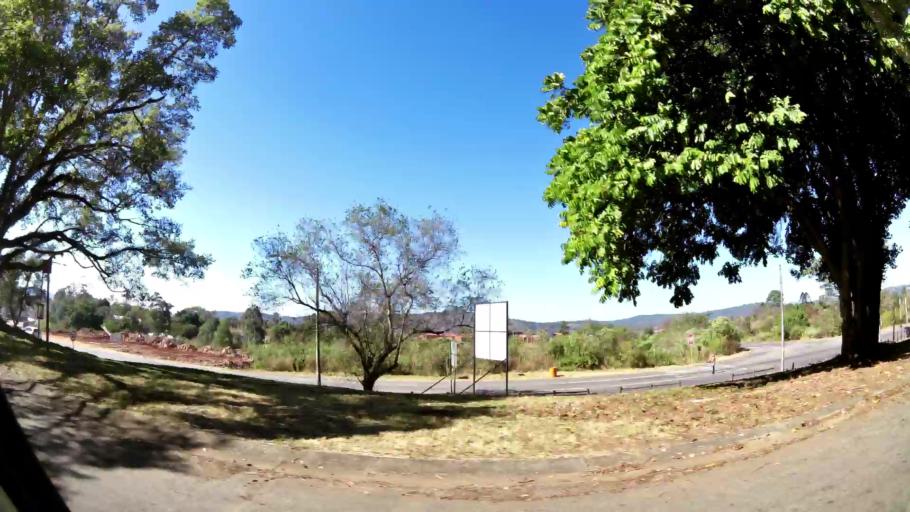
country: ZA
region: Limpopo
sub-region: Mopani District Municipality
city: Tzaneen
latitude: -23.8409
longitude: 30.1502
